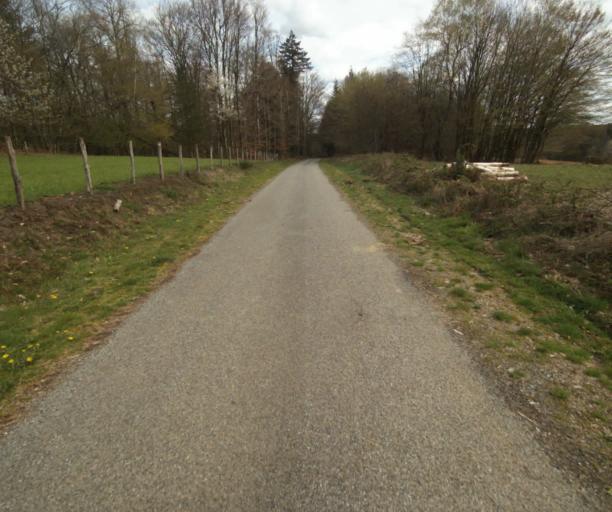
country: FR
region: Limousin
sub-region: Departement de la Correze
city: Argentat
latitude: 45.1873
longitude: 1.9153
